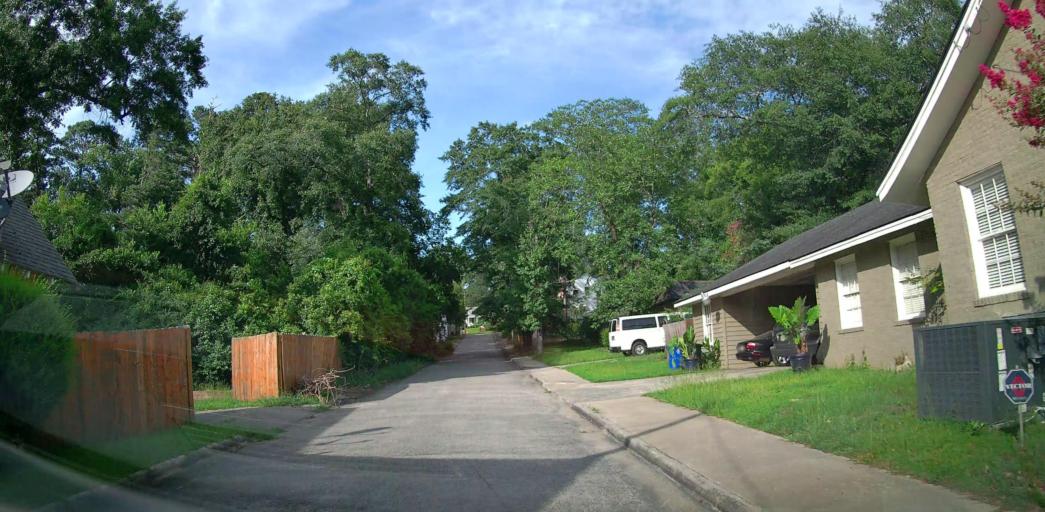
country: US
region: Georgia
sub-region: Bibb County
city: Macon
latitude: 32.8523
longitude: -83.6263
